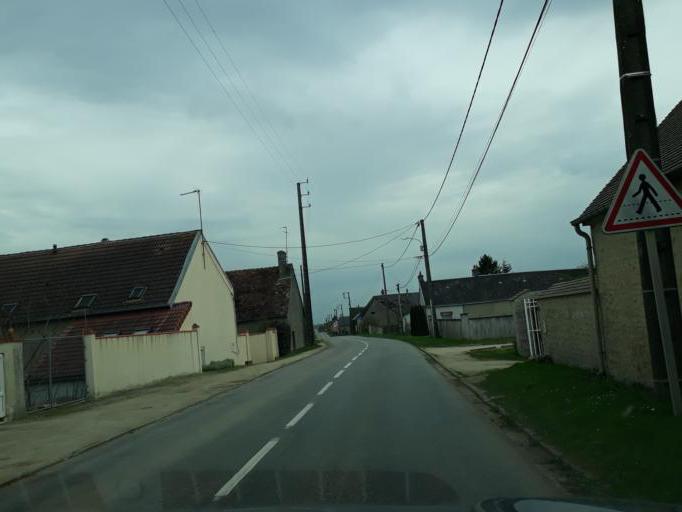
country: FR
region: Centre
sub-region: Departement du Loiret
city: Epieds-en-Beauce
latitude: 47.9192
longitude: 1.5969
